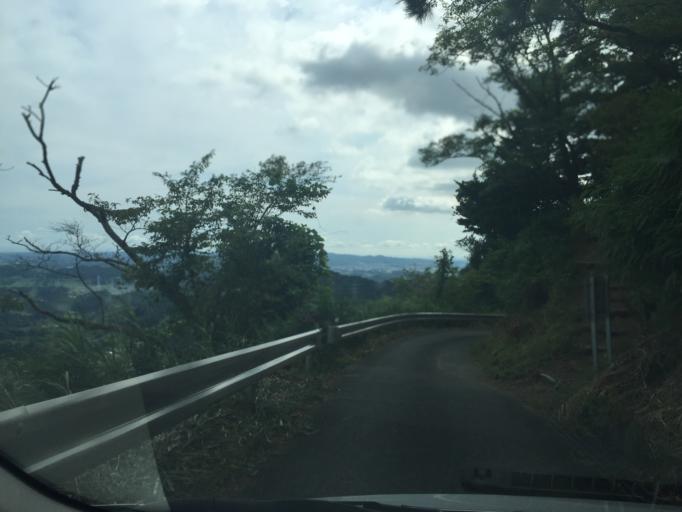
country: JP
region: Shizuoka
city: Kanaya
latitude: 34.8401
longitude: 138.0705
